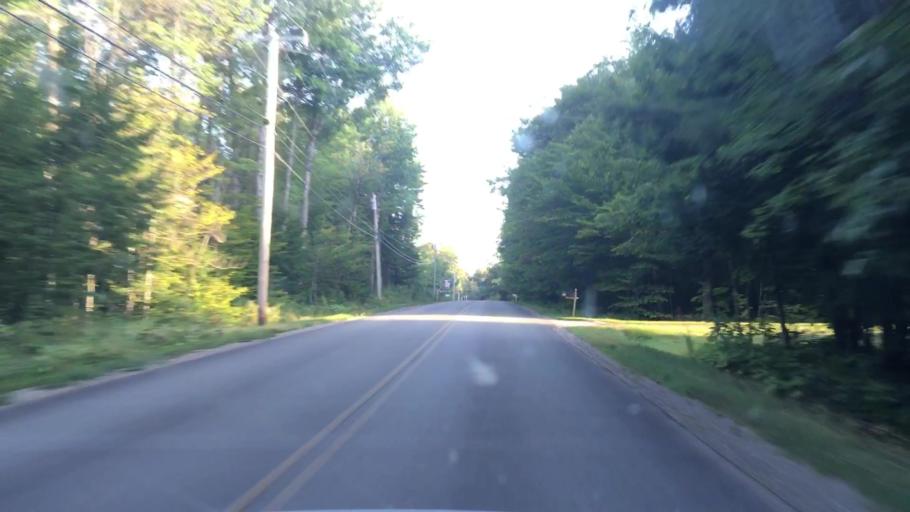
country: US
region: Maine
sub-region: Penobscot County
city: Hampden
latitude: 44.7164
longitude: -68.8869
